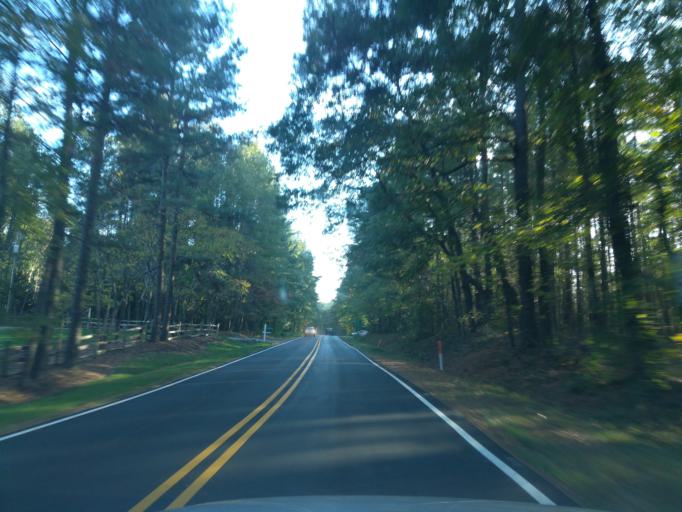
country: US
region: North Carolina
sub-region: Orange County
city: Chapel Hill
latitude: 35.9670
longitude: -79.0348
